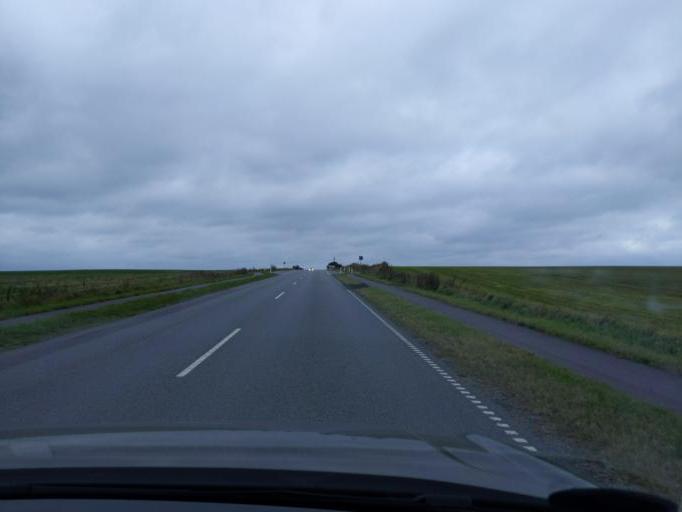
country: DK
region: North Denmark
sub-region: Mariagerfjord Kommune
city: Hobro
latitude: 56.5931
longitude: 9.7787
